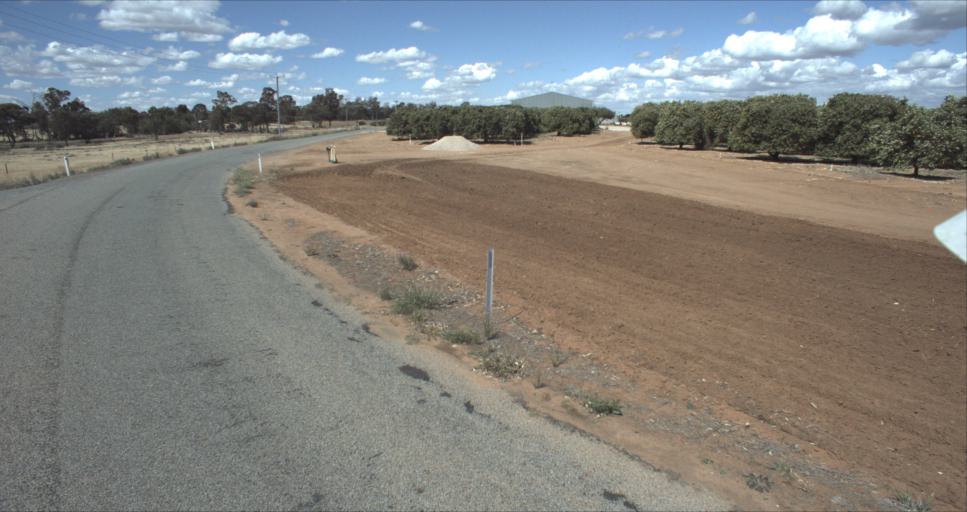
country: AU
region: New South Wales
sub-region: Leeton
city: Leeton
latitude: -34.5185
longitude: 146.2255
